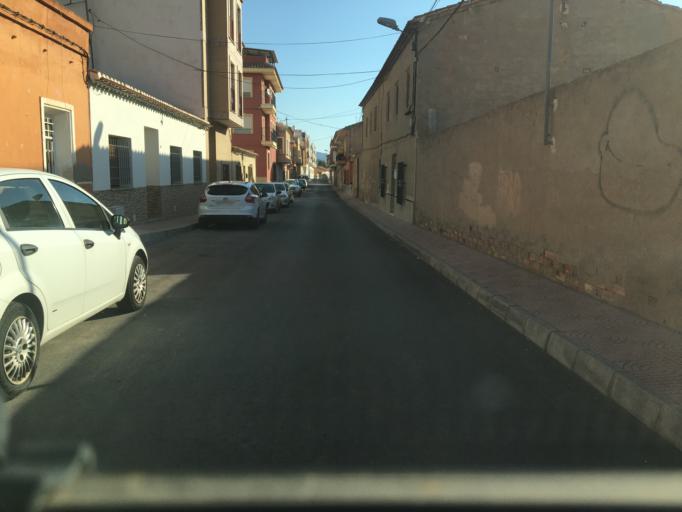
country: ES
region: Murcia
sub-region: Murcia
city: Puerto Lumbreras
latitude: 37.5653
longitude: -1.8082
